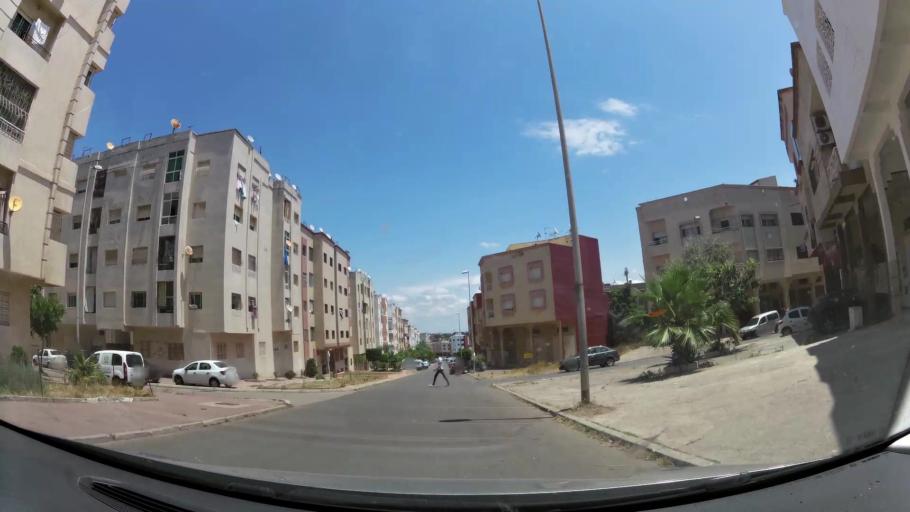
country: MA
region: Gharb-Chrarda-Beni Hssen
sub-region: Kenitra Province
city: Kenitra
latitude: 34.2558
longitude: -6.6185
